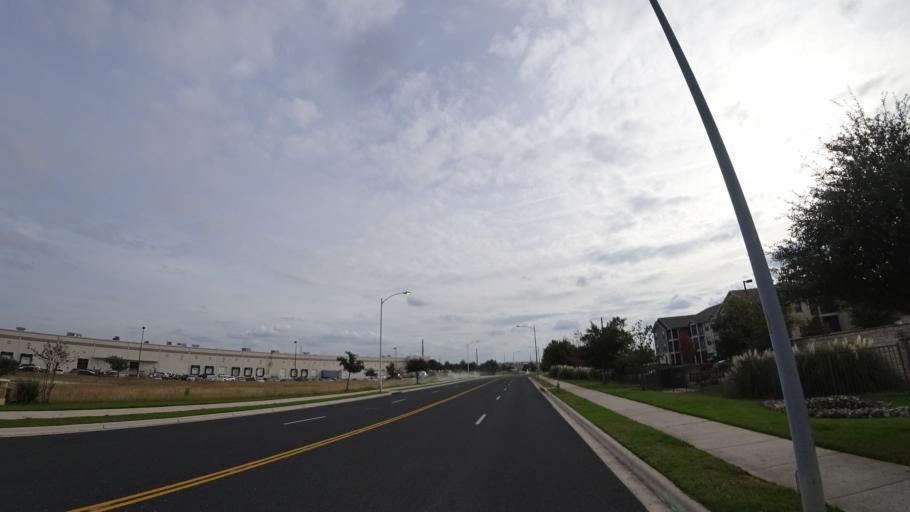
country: US
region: Texas
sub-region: Travis County
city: Wells Branch
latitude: 30.4240
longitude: -97.6651
